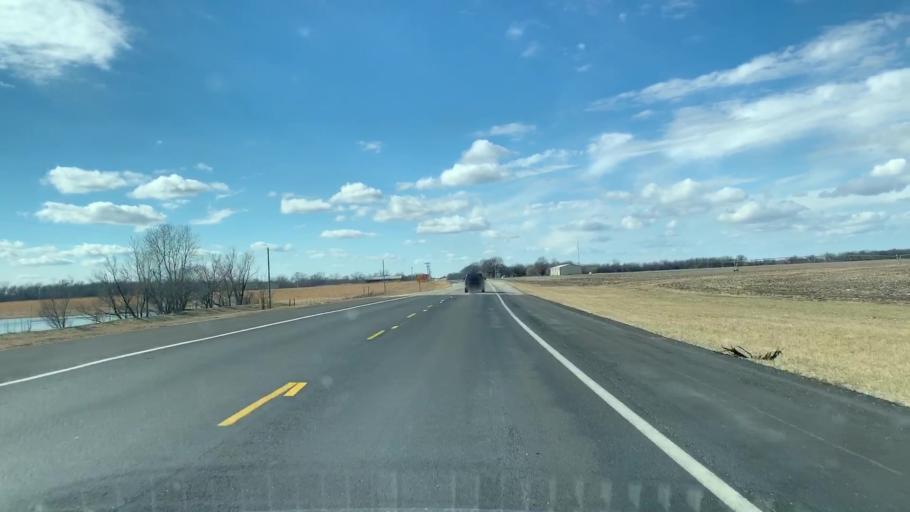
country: US
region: Kansas
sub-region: Labette County
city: Parsons
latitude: 37.3403
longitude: -95.1212
